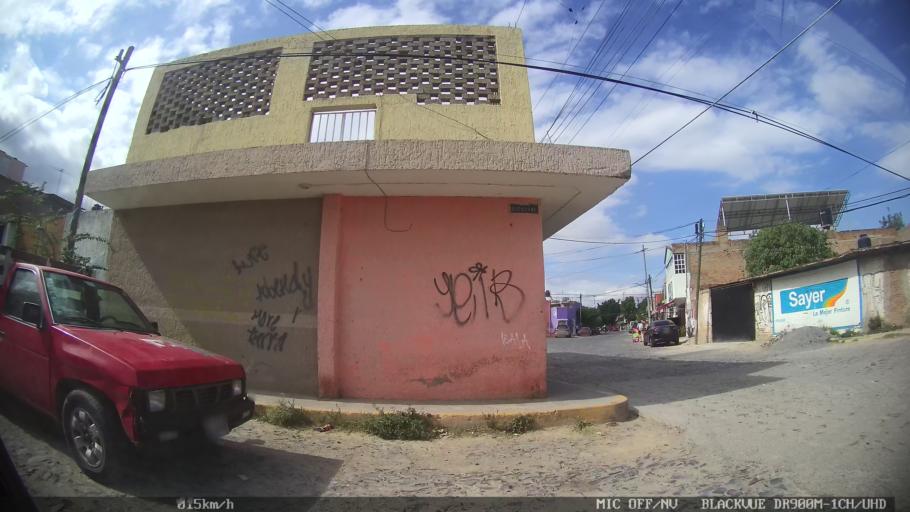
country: MX
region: Jalisco
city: Tlaquepaque
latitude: 20.6840
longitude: -103.2564
